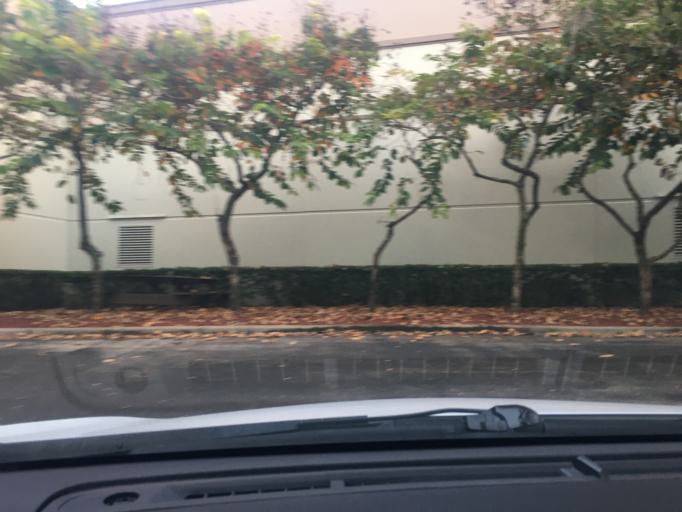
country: US
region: Florida
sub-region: Broward County
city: Dania Beach
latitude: 26.0713
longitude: -80.1796
